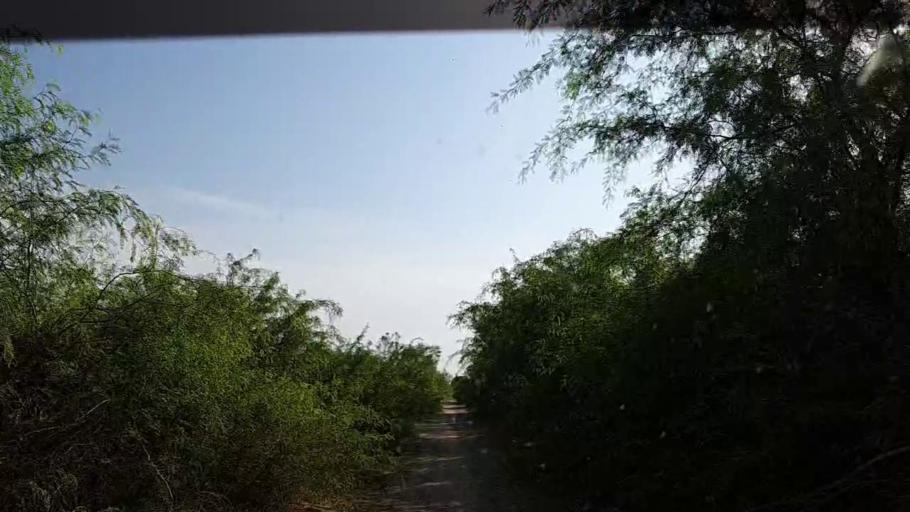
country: PK
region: Sindh
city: Adilpur
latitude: 27.9078
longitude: 69.2362
